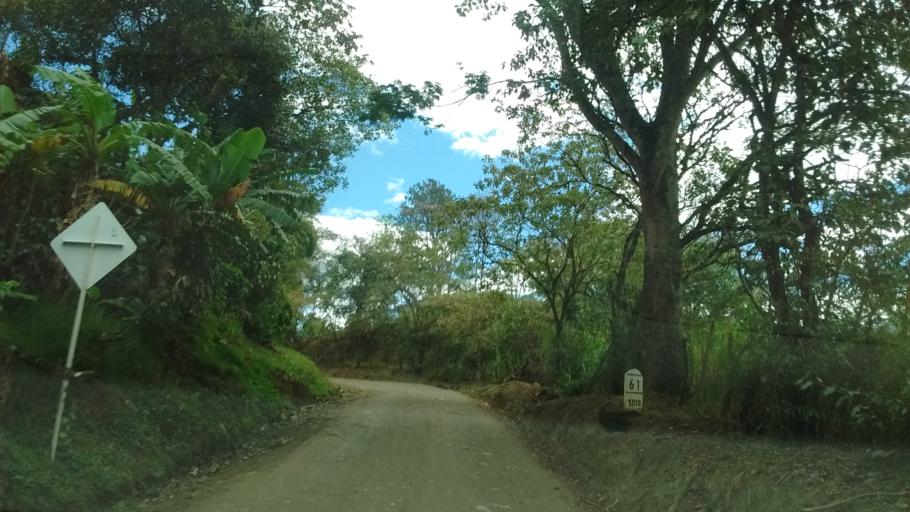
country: CO
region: Cauca
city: Almaguer
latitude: 1.8459
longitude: -76.9236
